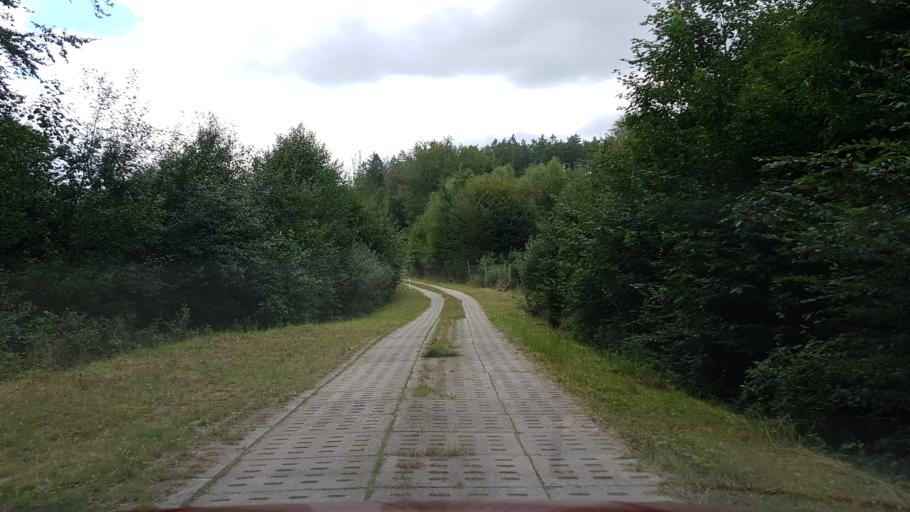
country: PL
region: West Pomeranian Voivodeship
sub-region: Powiat szczecinecki
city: Grzmiaca
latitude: 53.9642
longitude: 16.3949
